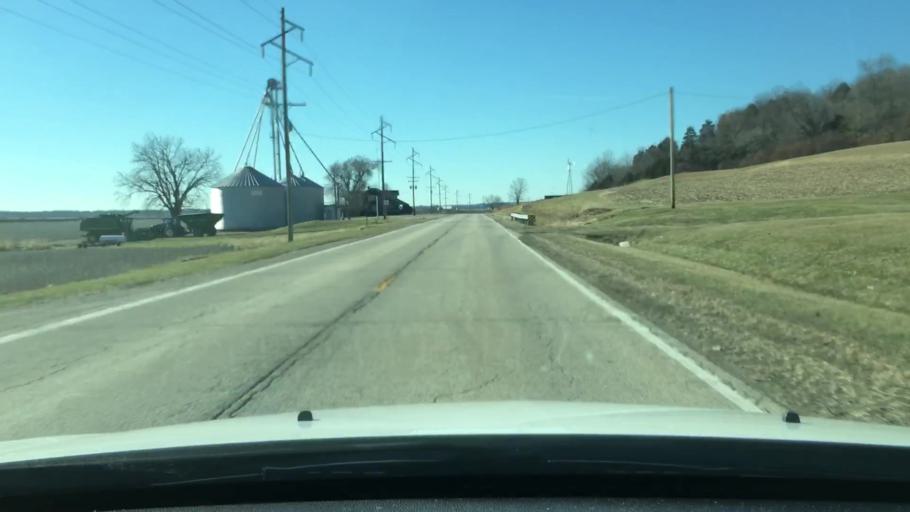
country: US
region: Illinois
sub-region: Fulton County
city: Astoria
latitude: 40.1826
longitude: -90.2220
